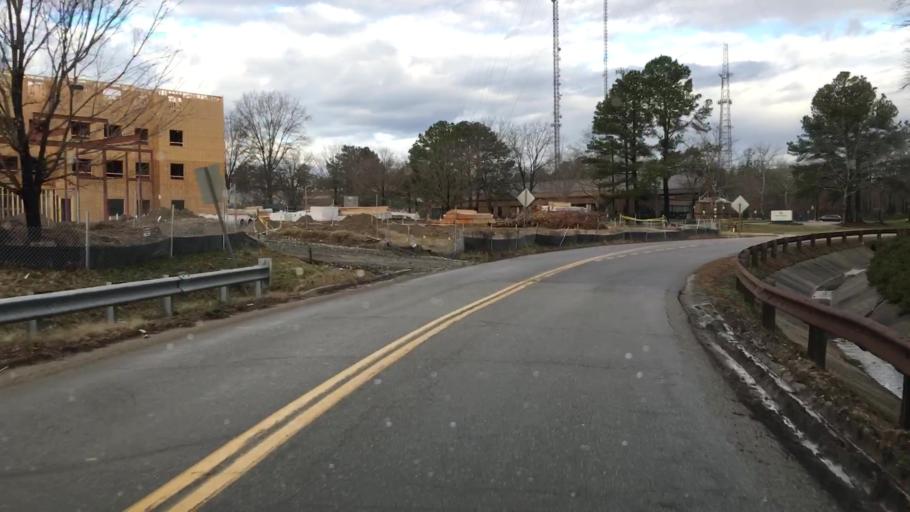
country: US
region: Virginia
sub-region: Chesterfield County
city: Bon Air
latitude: 37.5097
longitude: -77.5968
